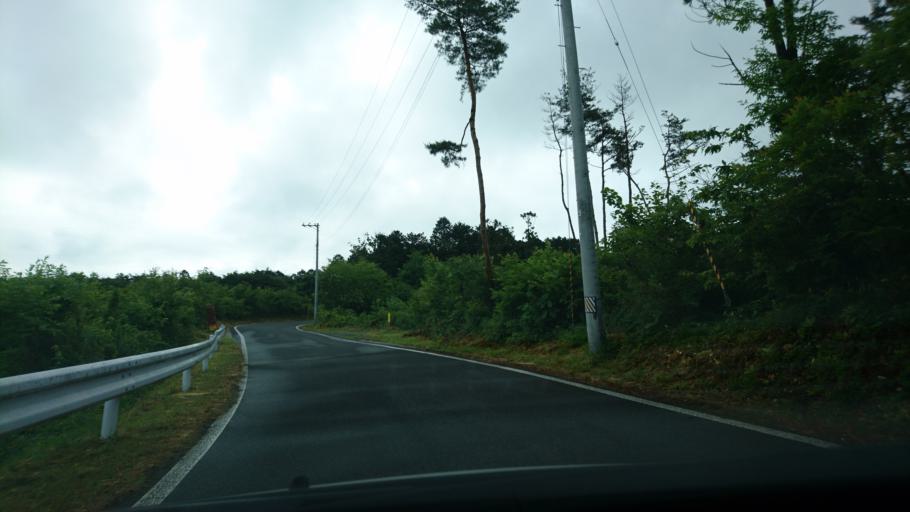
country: JP
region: Iwate
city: Ichinoseki
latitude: 38.9017
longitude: 141.1431
